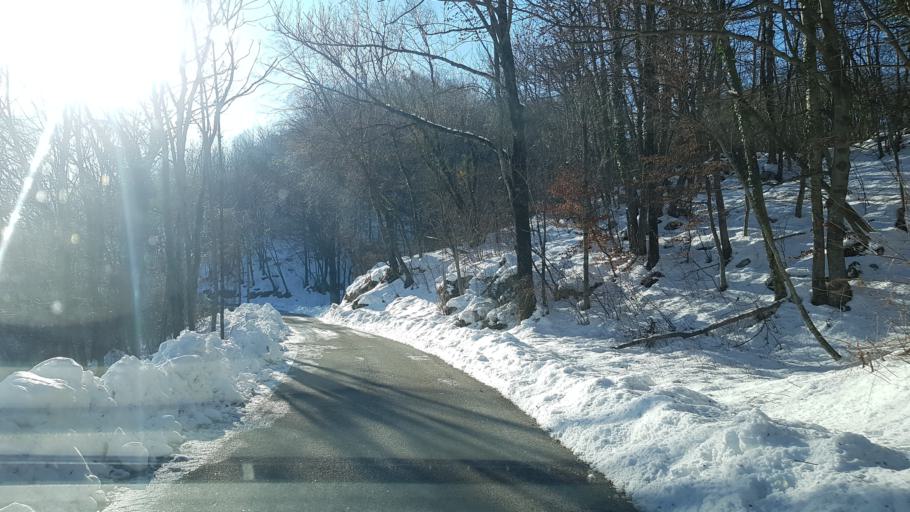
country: IT
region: Friuli Venezia Giulia
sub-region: Provincia di Udine
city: Forgaria nel Friuli
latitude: 46.2645
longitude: 12.9965
